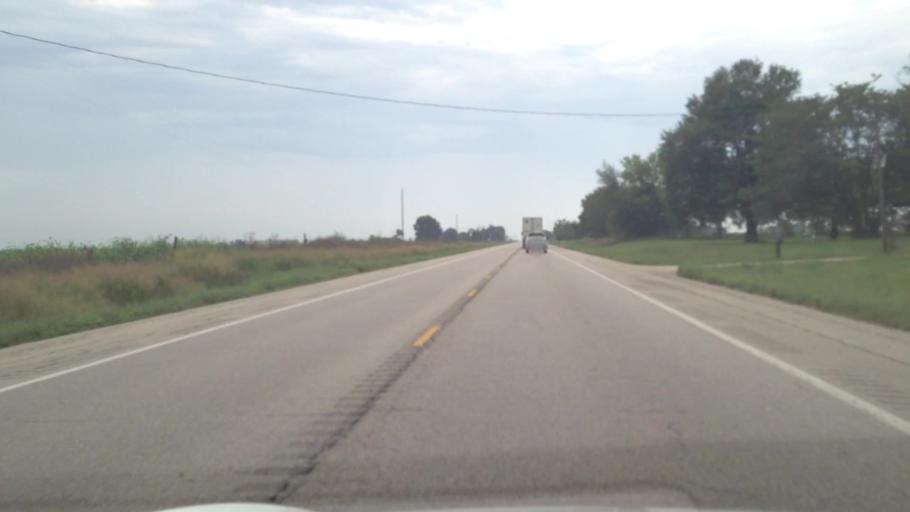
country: US
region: Kansas
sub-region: Crawford County
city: Pittsburg
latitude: 37.2854
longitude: -94.7054
